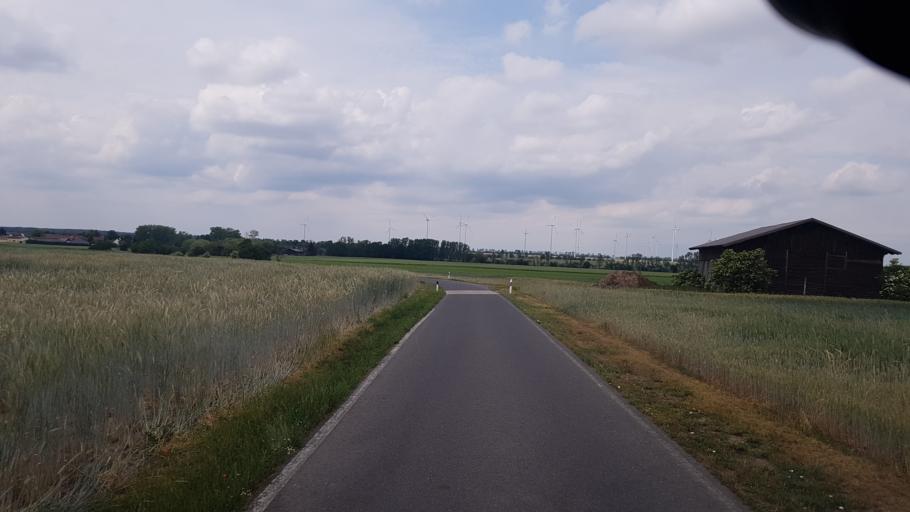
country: DE
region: Brandenburg
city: Ihlow
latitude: 51.8826
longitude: 13.3638
